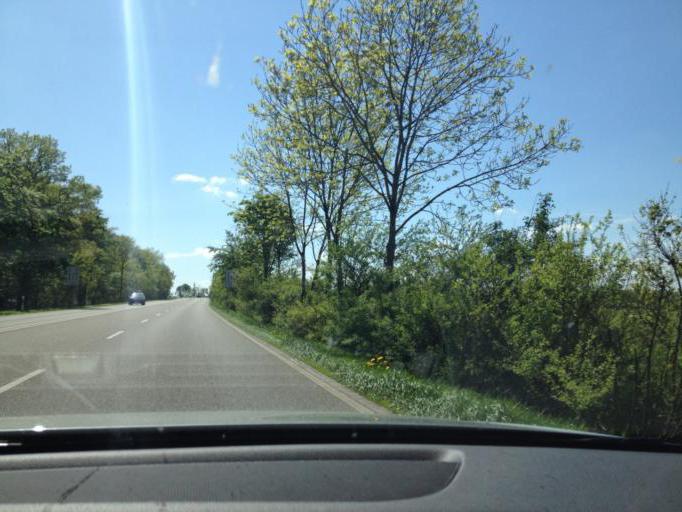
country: DE
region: North Rhine-Westphalia
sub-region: Regierungsbezirk Koln
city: Dahlem
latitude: 50.4164
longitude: 6.5844
